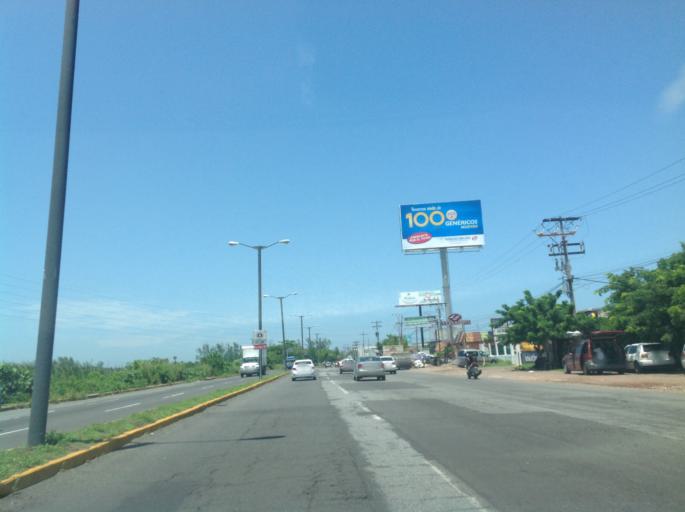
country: MX
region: Veracruz
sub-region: Veracruz
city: Hacienda Sotavento
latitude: 19.1428
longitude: -96.1461
